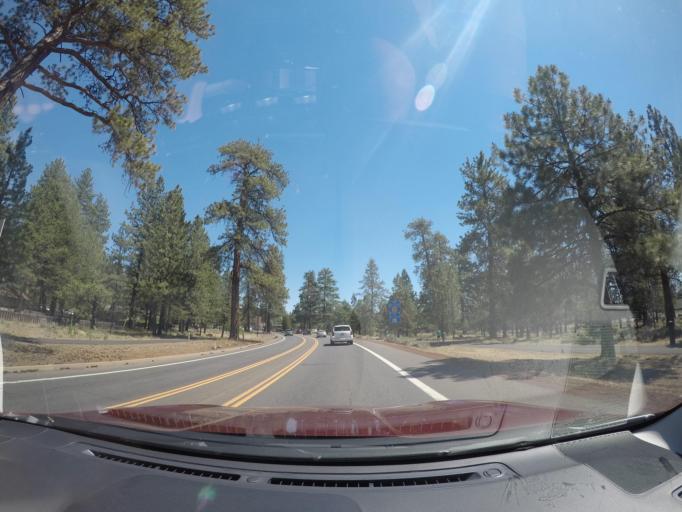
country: US
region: Oregon
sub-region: Deschutes County
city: Sisters
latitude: 44.2923
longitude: -121.5567
